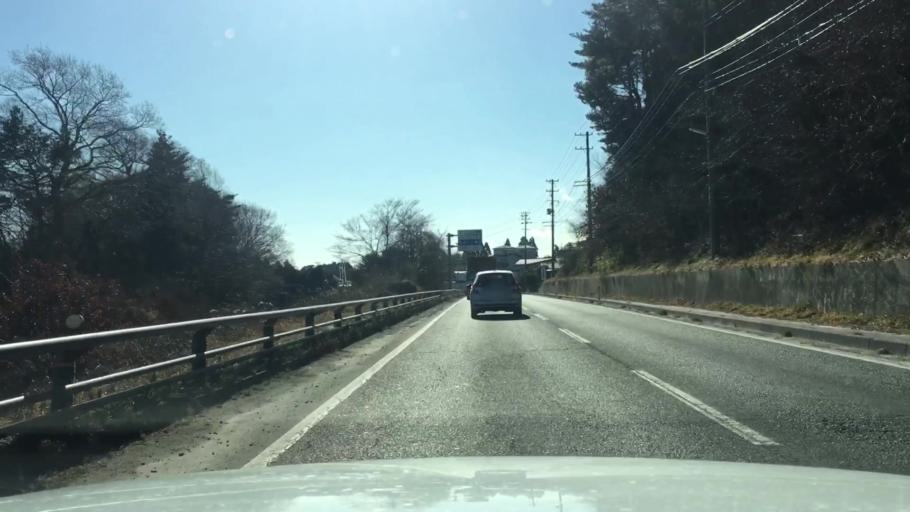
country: JP
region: Iwate
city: Yamada
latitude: 39.4414
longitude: 141.9718
